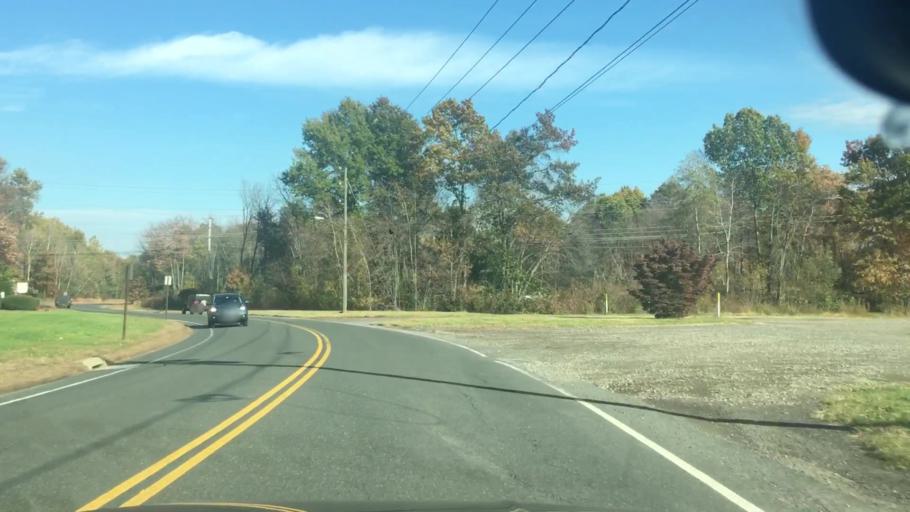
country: US
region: Massachusetts
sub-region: Hampden County
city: East Longmeadow
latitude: 42.0385
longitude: -72.5343
